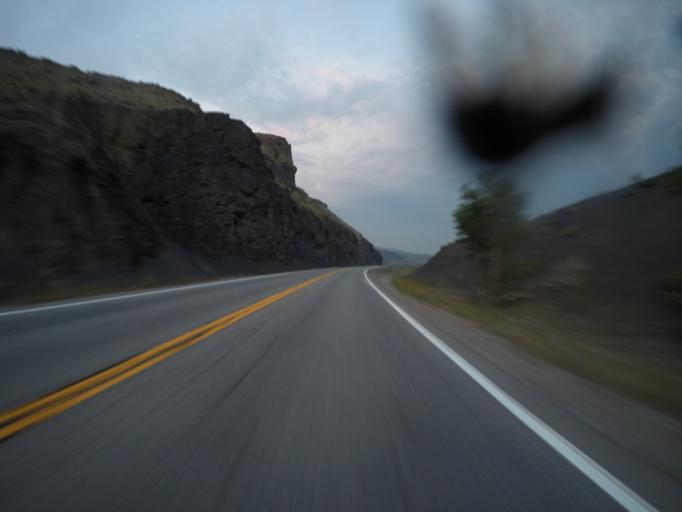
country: US
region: Colorado
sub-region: Grand County
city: Kremmling
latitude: 39.8592
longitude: -106.2496
